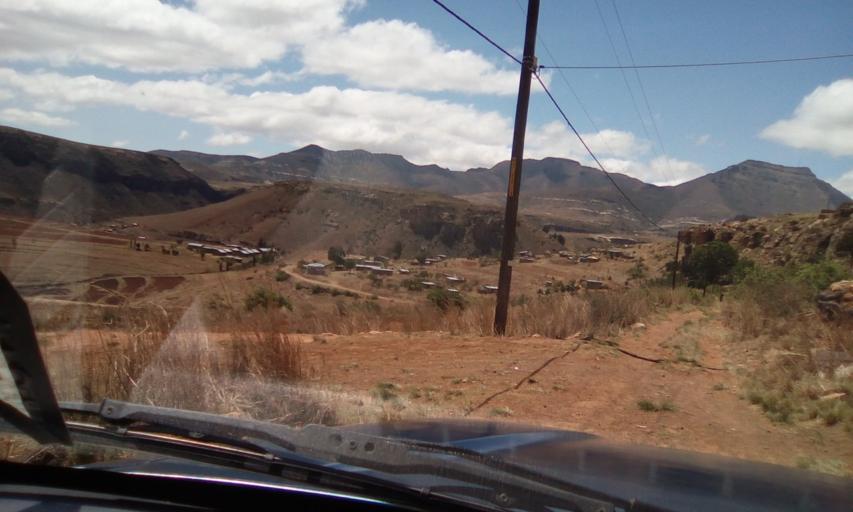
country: LS
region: Qacha's Nek
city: Qacha's Nek
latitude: -30.0686
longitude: 28.6349
